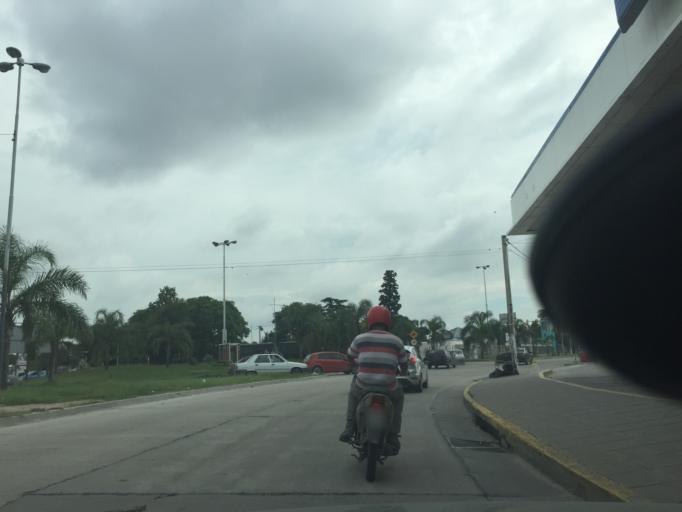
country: AR
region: Cordoba
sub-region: Departamento de Capital
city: Cordoba
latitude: -31.4503
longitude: -64.2001
